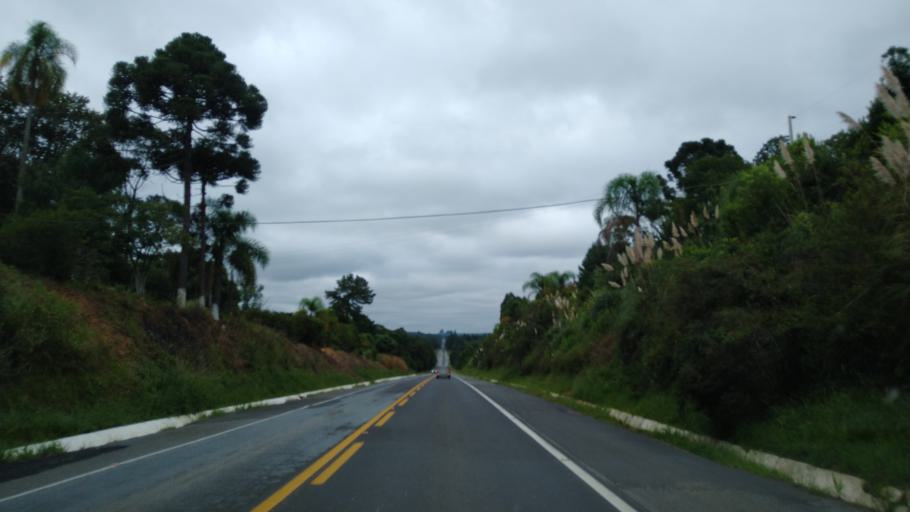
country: BR
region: Santa Catarina
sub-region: Tres Barras
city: Tres Barras
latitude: -26.1717
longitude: -50.1585
